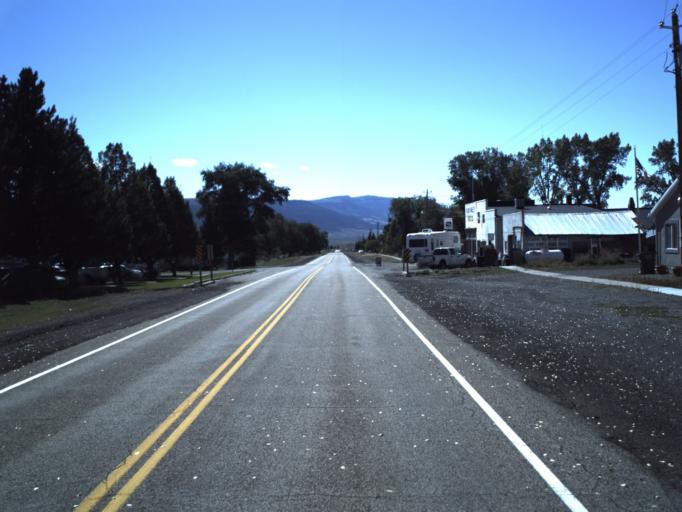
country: US
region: Utah
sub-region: Wayne County
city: Loa
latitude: 38.5112
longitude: -111.8814
